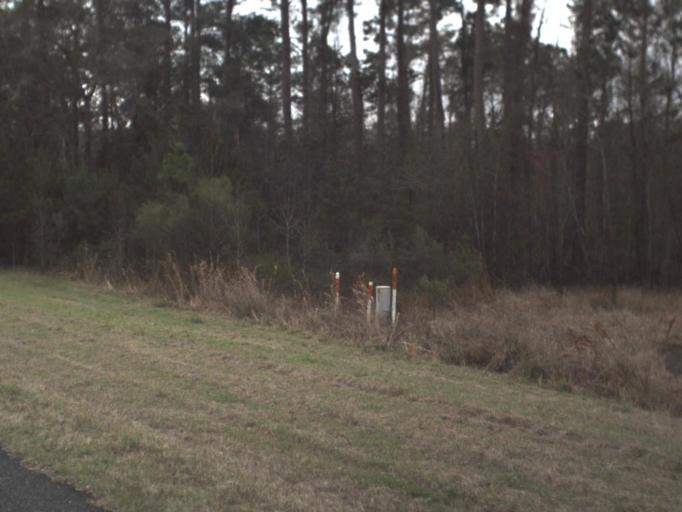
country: US
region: Florida
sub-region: Jefferson County
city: Monticello
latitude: 30.3794
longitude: -83.8172
